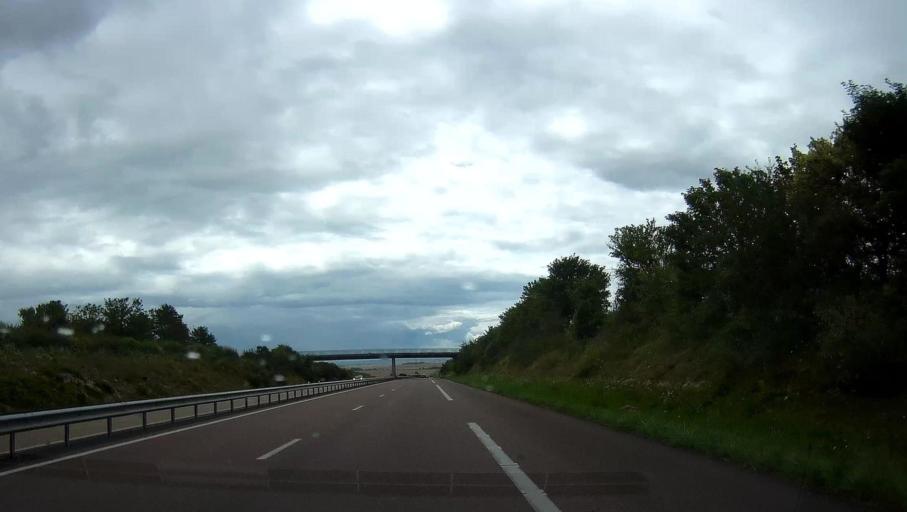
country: FR
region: Champagne-Ardenne
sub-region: Departement de l'Aube
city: Creney-pres-Troyes
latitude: 48.3635
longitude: 4.1613
